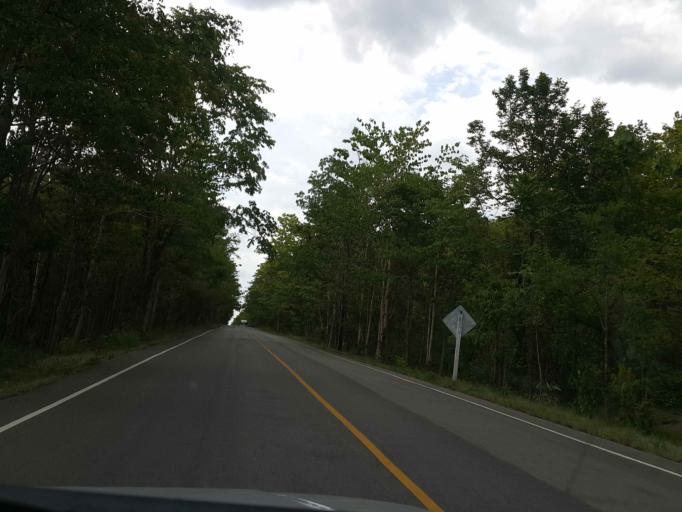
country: TH
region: Sukhothai
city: Thung Saliam
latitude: 17.4014
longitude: 99.3910
